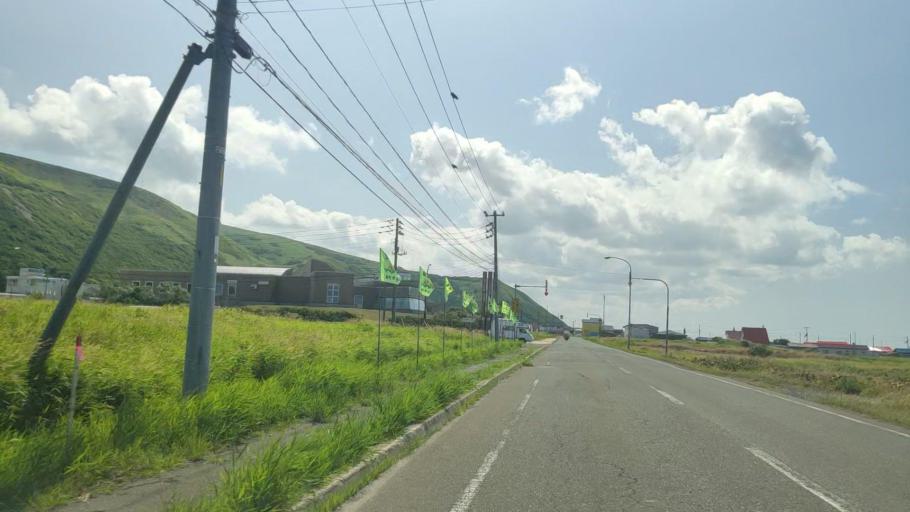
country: JP
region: Hokkaido
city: Wakkanai
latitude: 45.4222
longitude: 141.6370
